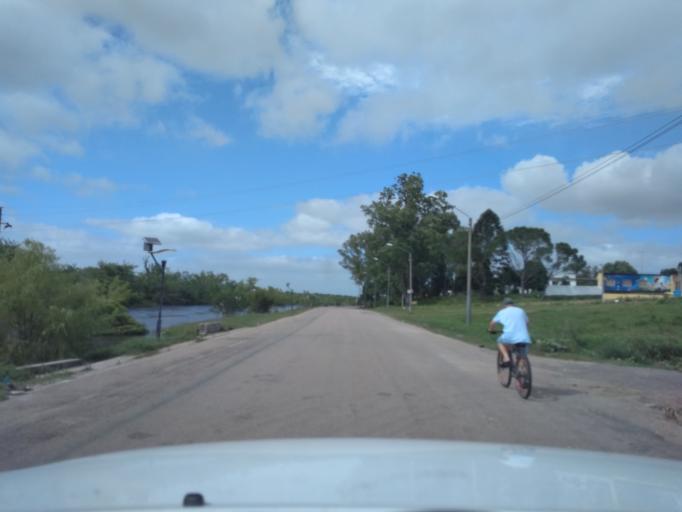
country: UY
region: Florida
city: Florida
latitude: -34.1057
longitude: -56.2046
